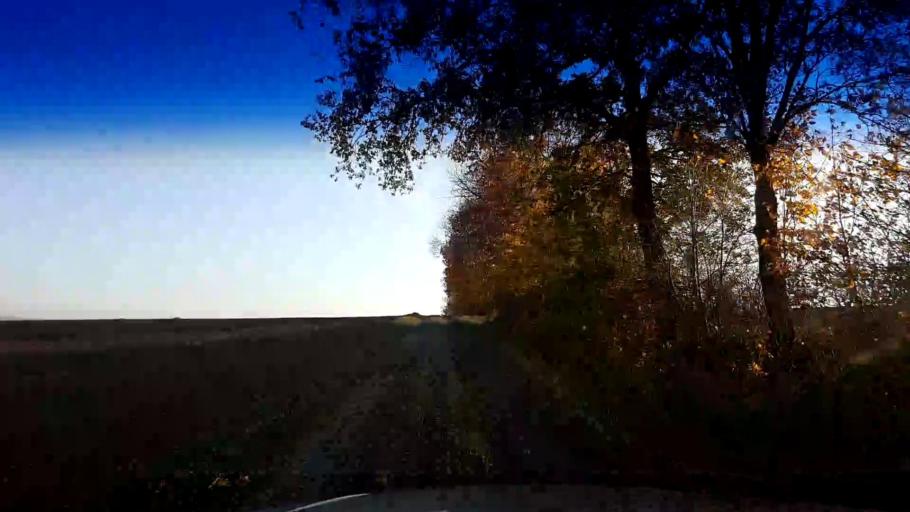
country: DE
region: Bavaria
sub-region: Upper Franconia
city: Memmelsdorf
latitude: 49.9720
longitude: 10.9721
